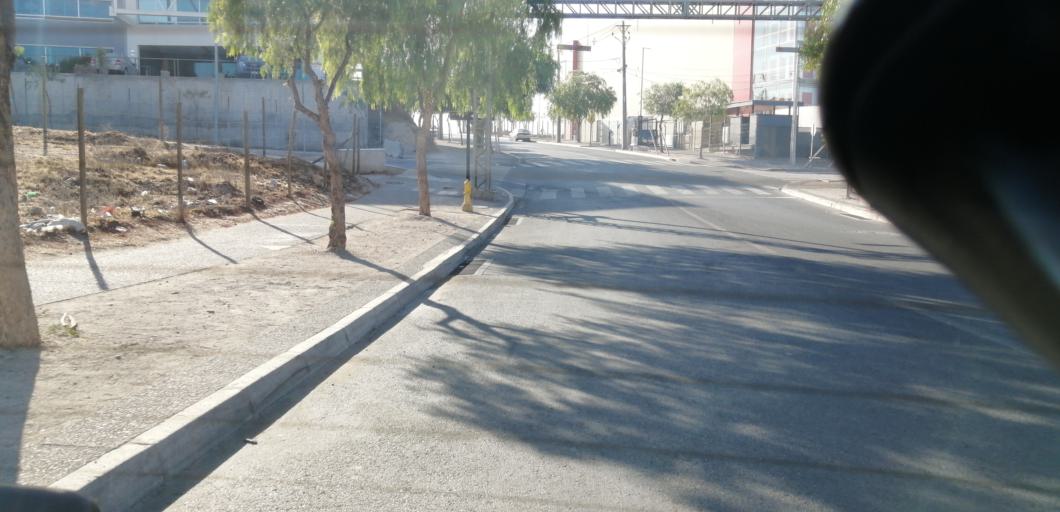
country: CL
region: Santiago Metropolitan
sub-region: Provincia de Santiago
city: Lo Prado
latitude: -33.4351
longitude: -70.7869
